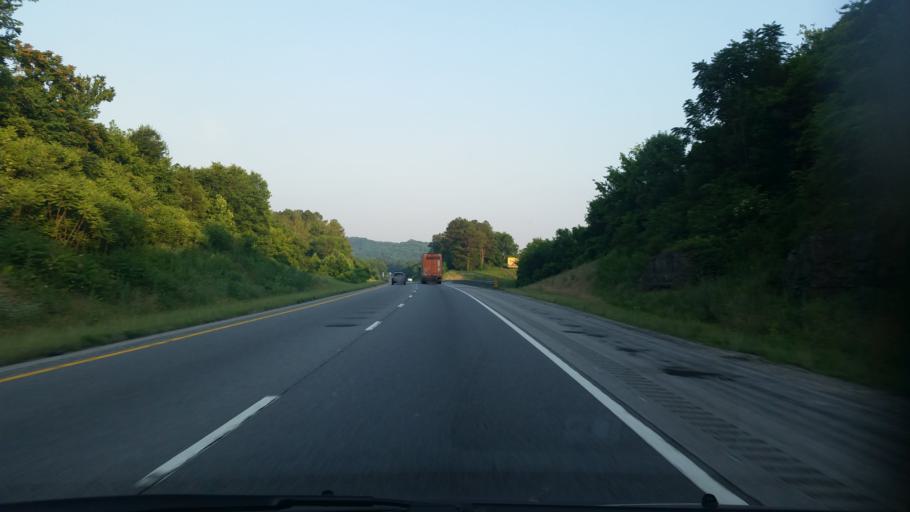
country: US
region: Tennessee
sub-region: Smith County
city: Gordonsville
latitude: 36.1573
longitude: -85.8816
